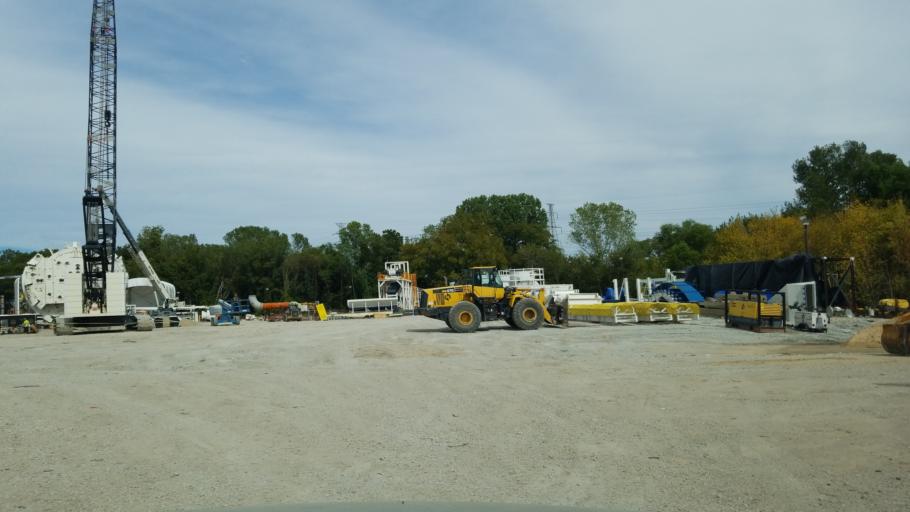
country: US
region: Texas
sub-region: Dallas County
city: Dallas
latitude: 32.7634
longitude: -96.7320
